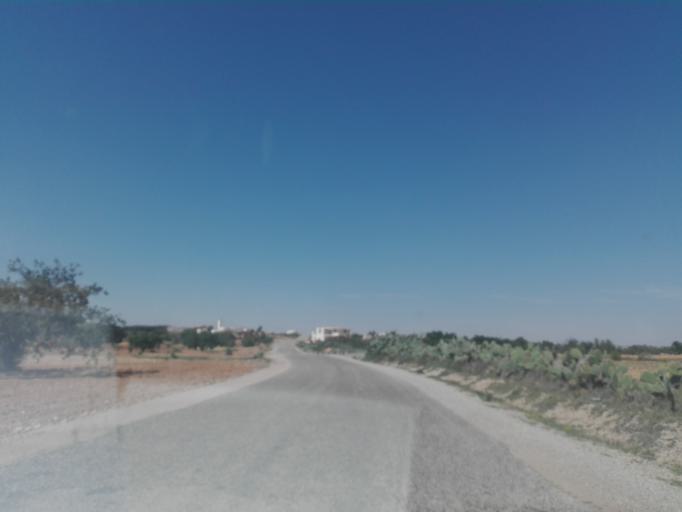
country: TN
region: Safaqis
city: Bi'r `Ali Bin Khalifah
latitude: 34.6691
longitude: 10.3567
